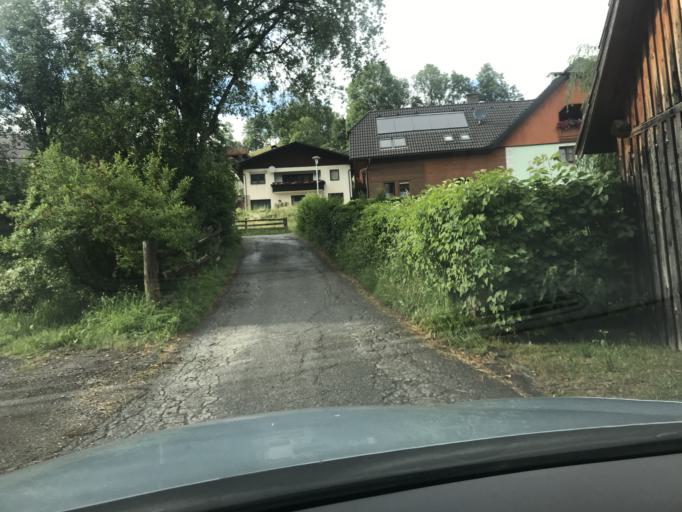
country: AT
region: Styria
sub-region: Politischer Bezirk Murau
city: Sankt Peter am Kammersberg
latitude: 47.1897
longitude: 14.1719
